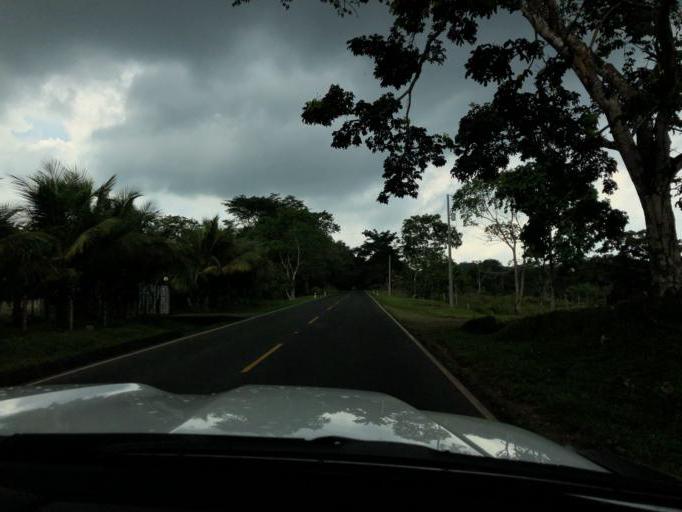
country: NI
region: Chontales
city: Villa Sandino
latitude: 11.9905
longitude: -84.8205
